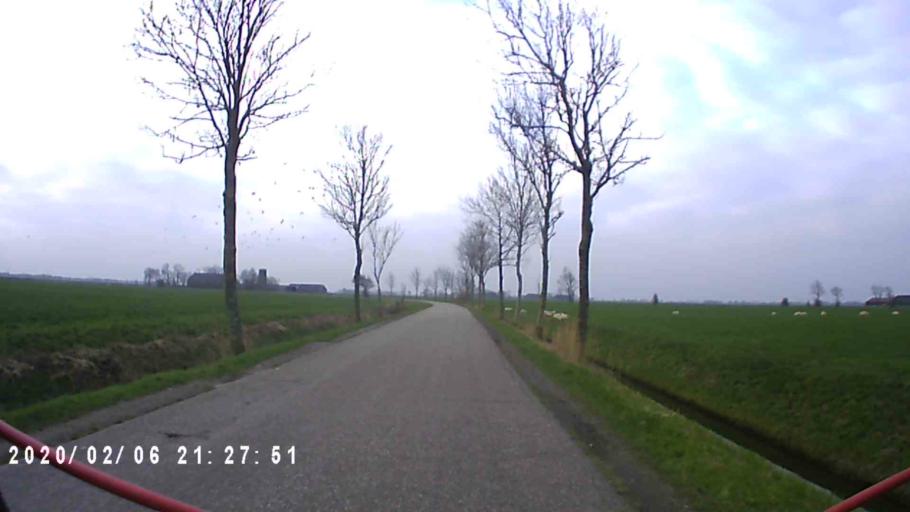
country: NL
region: Groningen
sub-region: Gemeente Zuidhorn
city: Oldehove
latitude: 53.2826
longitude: 6.3780
